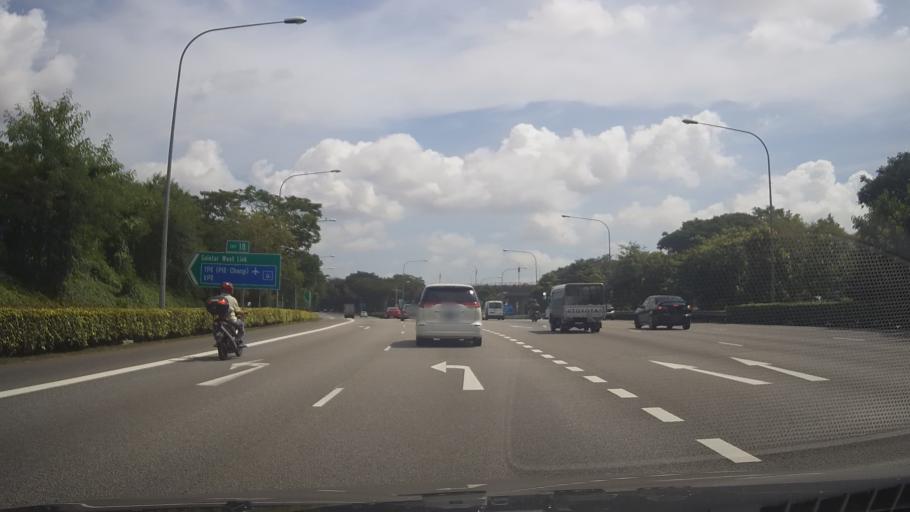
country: MY
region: Johor
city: Kampung Pasir Gudang Baru
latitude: 1.3969
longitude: 103.8514
